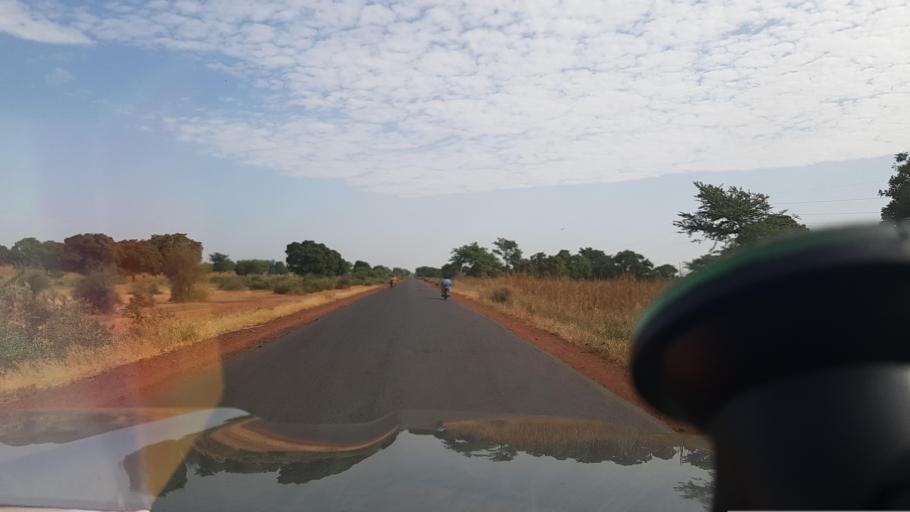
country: ML
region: Segou
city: Segou
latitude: 13.5151
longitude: -6.1394
